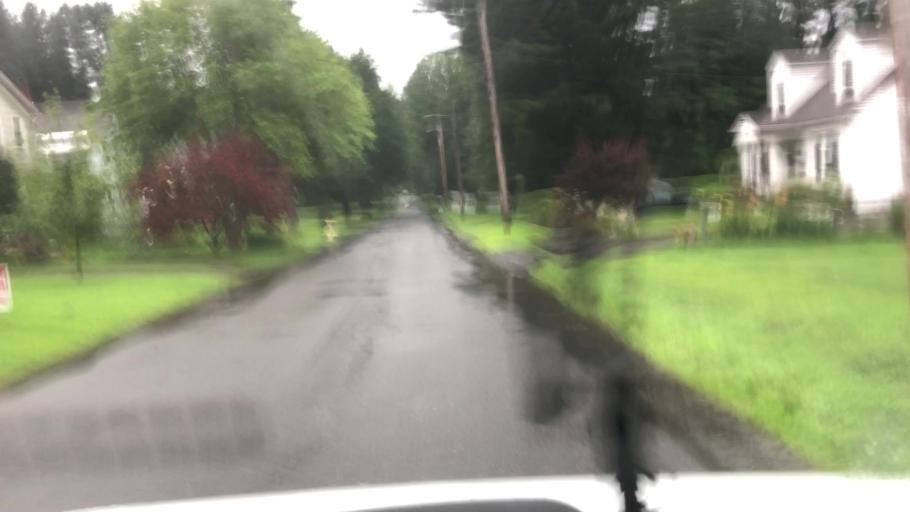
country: US
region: Massachusetts
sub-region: Hampshire County
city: Northampton
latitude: 42.3284
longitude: -72.6753
